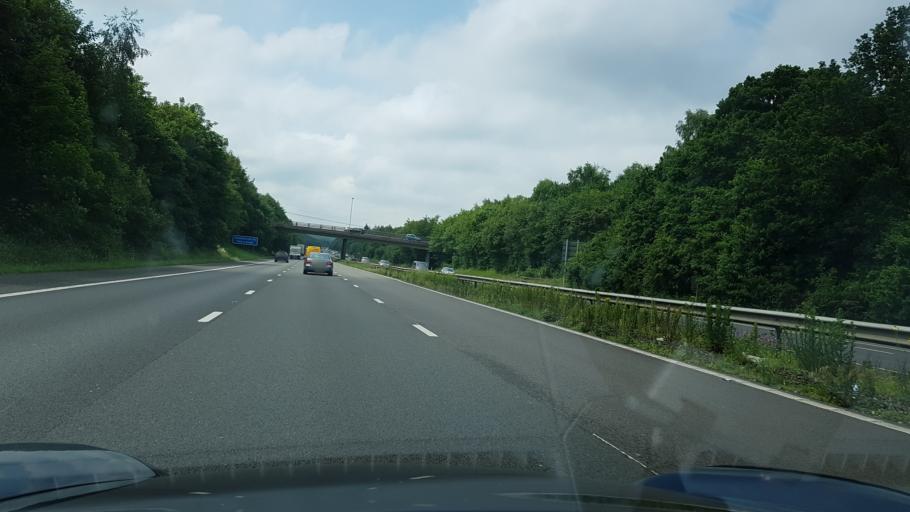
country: GB
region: England
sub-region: West Sussex
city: Maidenbower
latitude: 51.1048
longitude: -0.1436
